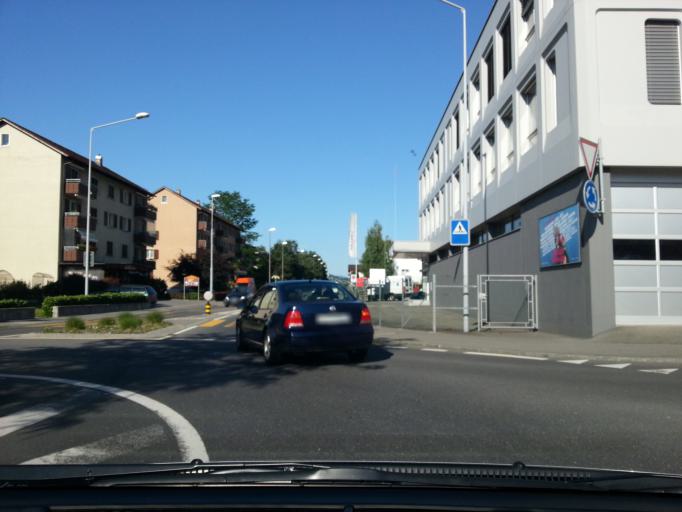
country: CH
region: Lucerne
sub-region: Lucerne-Stadt District
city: Littau
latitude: 47.0497
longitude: 8.2656
